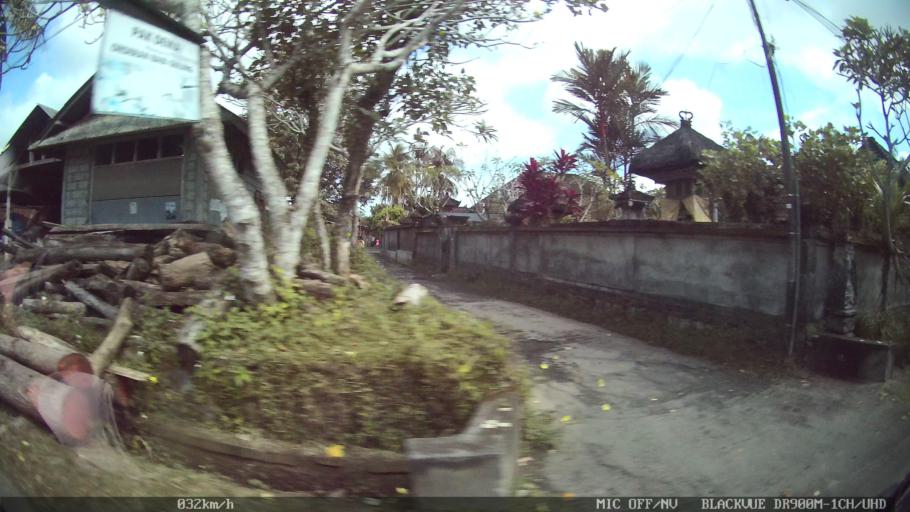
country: ID
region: Bali
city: Banjar Pesalakan
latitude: -8.5068
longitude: 115.3113
